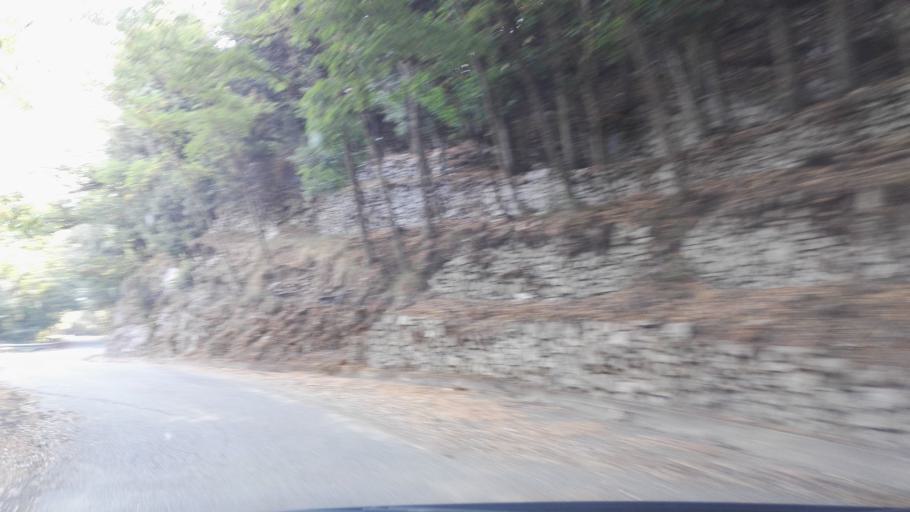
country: IT
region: Calabria
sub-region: Provincia di Vibo-Valentia
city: Nardodipace
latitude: 38.4570
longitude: 16.3479
